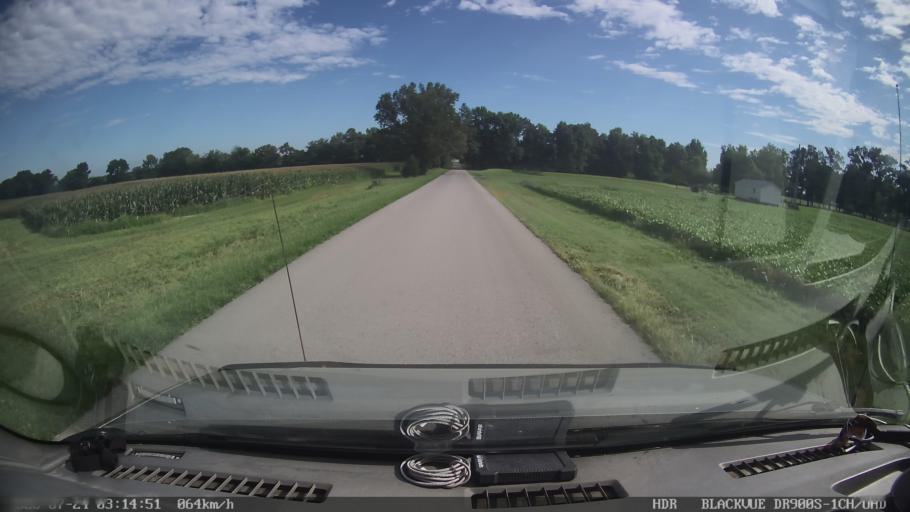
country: US
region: Kentucky
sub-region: Todd County
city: Guthrie
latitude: 36.6911
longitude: -87.1708
